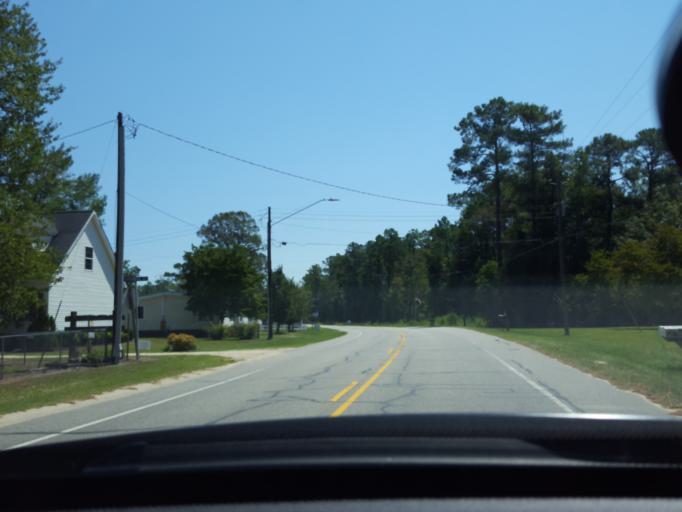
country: US
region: North Carolina
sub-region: Bladen County
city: Elizabethtown
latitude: 34.6332
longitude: -78.5061
